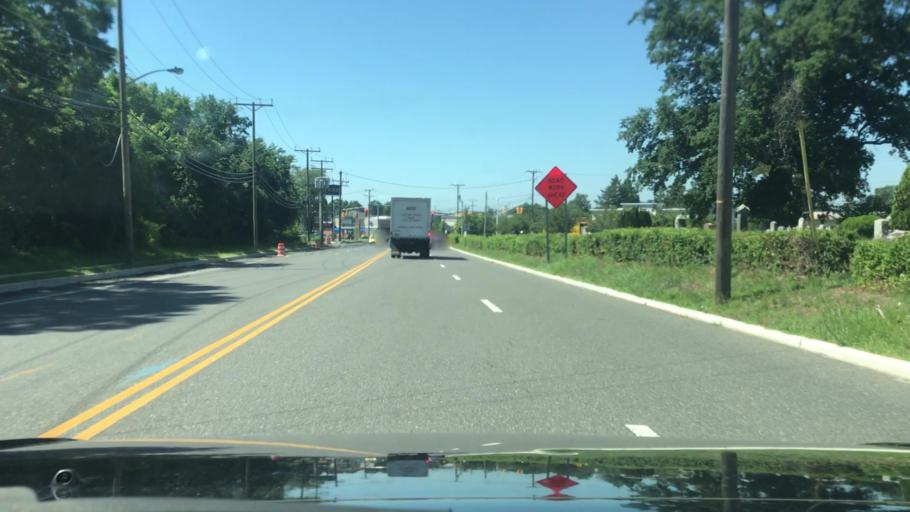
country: US
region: New Jersey
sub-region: Ocean County
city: Toms River
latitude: 39.9683
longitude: -74.2018
